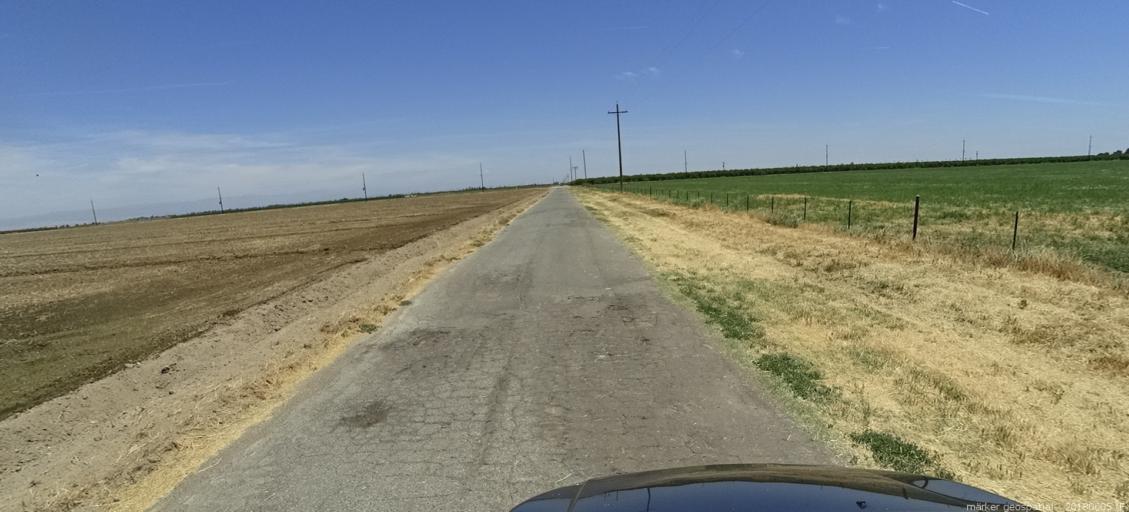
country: US
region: California
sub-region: Madera County
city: Chowchilla
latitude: 37.0982
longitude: -120.3151
